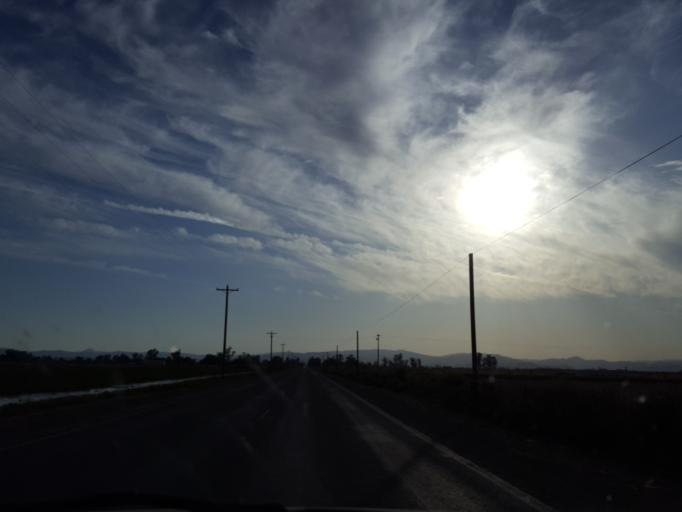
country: US
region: California
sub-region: Merced County
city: Los Banos
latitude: 37.1001
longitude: -120.9109
